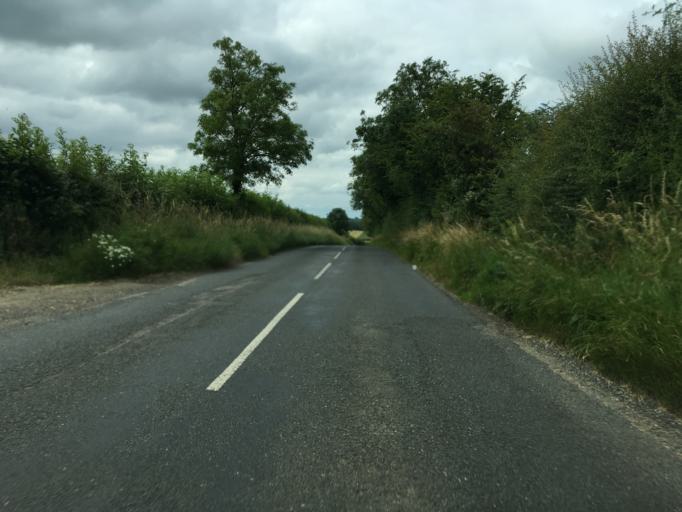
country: GB
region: England
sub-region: Oxfordshire
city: Shipton under Wychwood
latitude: 51.9079
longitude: -1.5973
